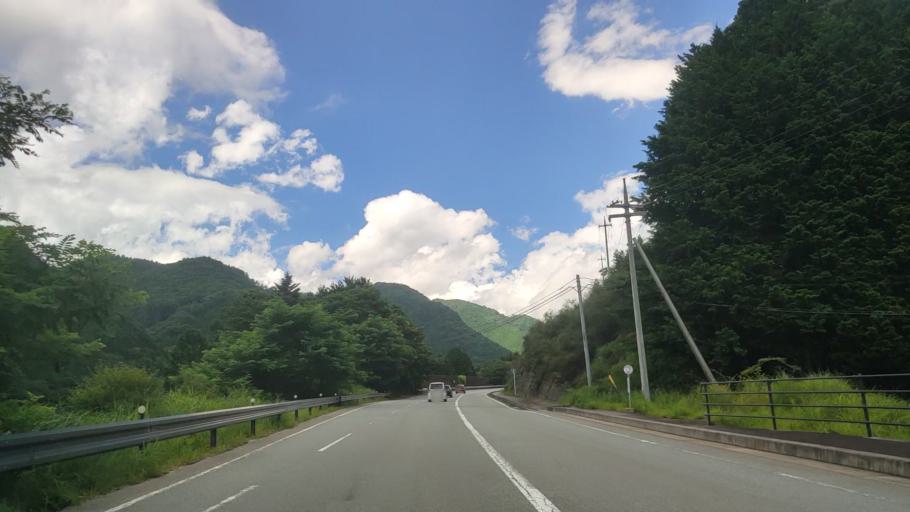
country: JP
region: Yamanashi
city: Enzan
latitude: 35.8100
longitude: 138.7515
